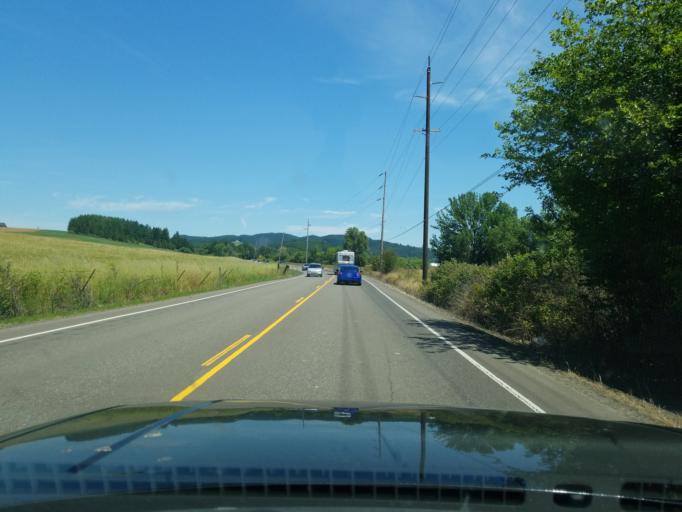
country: US
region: Oregon
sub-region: Yamhill County
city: Yamhill
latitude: 45.3567
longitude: -123.1698
